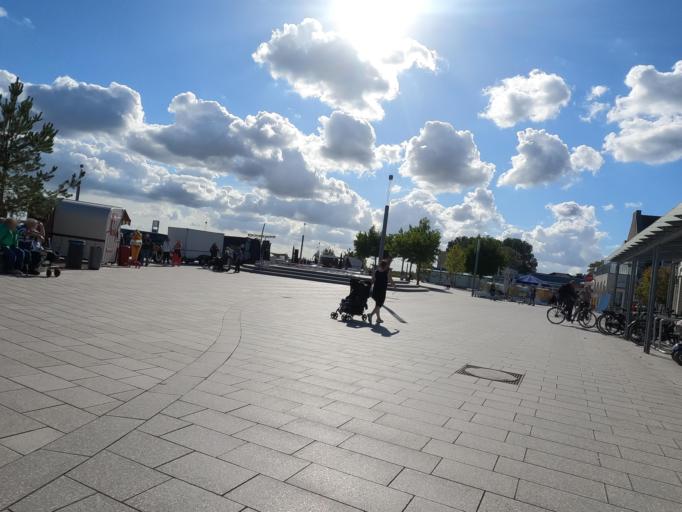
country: DE
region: Schleswig-Holstein
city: Grossenbrode
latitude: 54.3585
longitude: 11.0887
